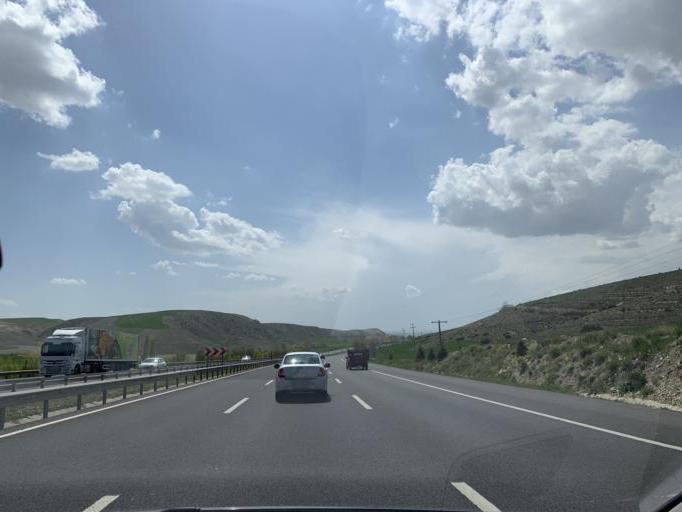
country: TR
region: Ankara
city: Temelli
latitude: 39.7667
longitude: 32.4830
